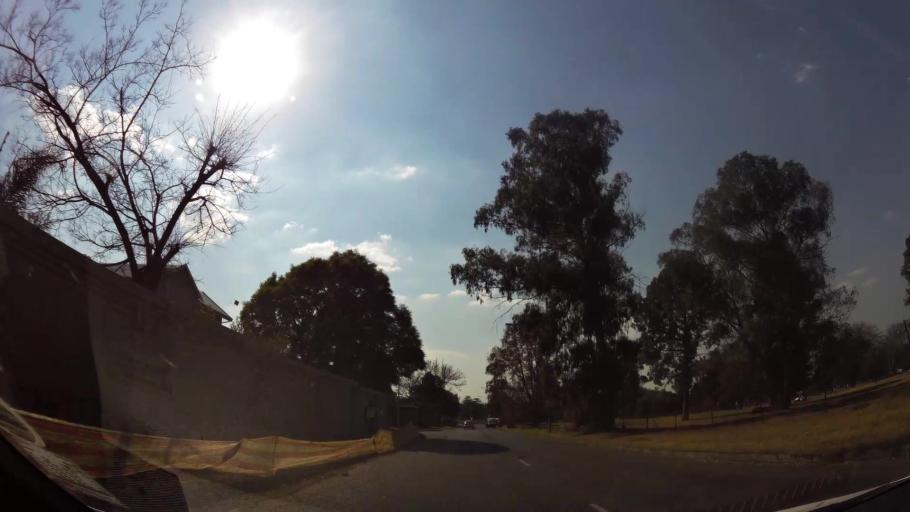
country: ZA
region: Gauteng
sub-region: Ekurhuleni Metropolitan Municipality
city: Benoni
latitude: -26.1832
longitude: 28.2926
